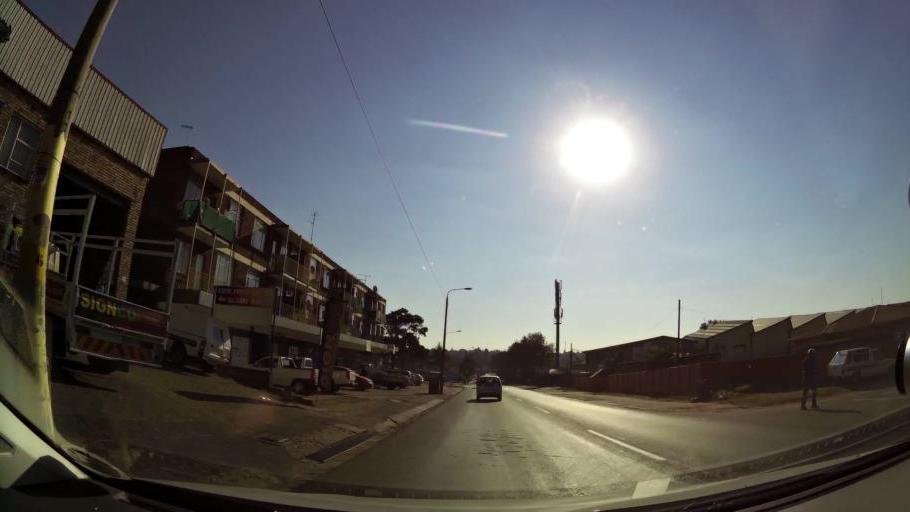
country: ZA
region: Gauteng
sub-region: City of Johannesburg Metropolitan Municipality
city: Modderfontein
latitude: -26.1360
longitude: 28.1607
